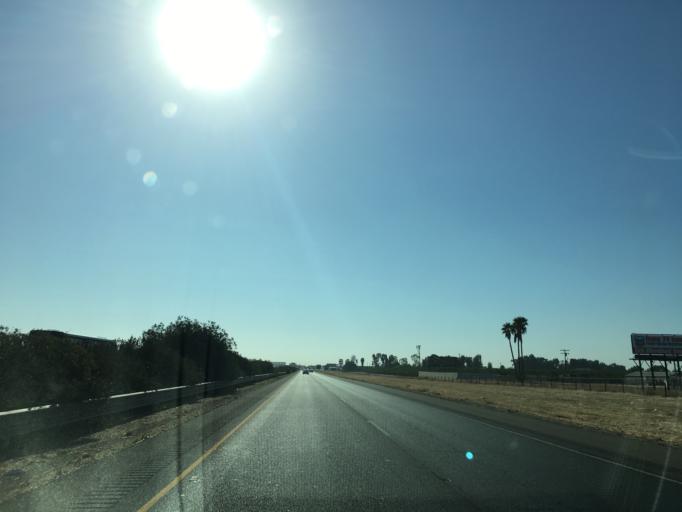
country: US
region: California
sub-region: Madera County
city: Fairmead
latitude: 37.0296
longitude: -120.1416
